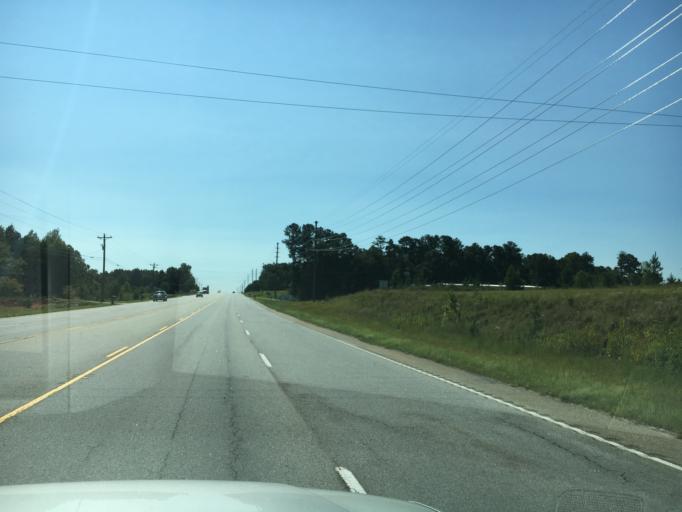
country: US
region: South Carolina
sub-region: Spartanburg County
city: Roebuck
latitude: 34.8587
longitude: -82.0203
